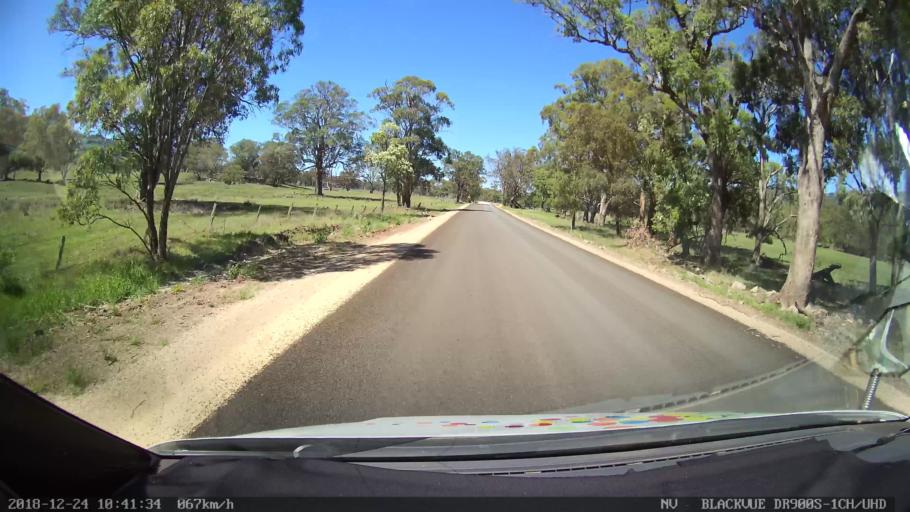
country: AU
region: New South Wales
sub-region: Upper Hunter Shire
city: Merriwa
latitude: -31.8700
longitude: 150.4583
